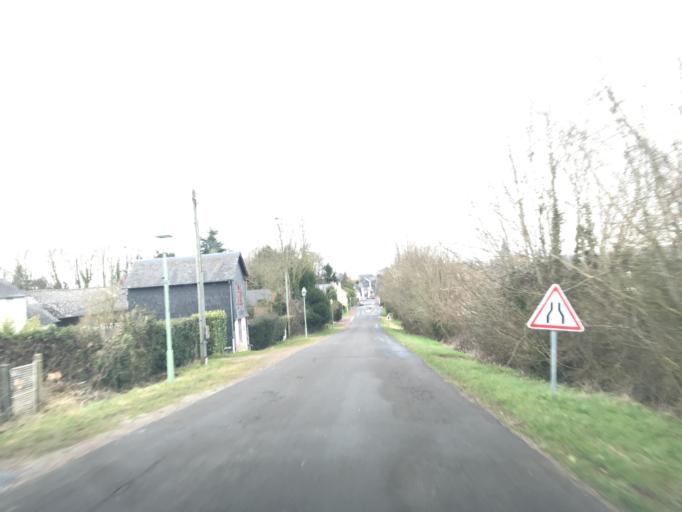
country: FR
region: Lower Normandy
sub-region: Departement du Calvados
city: Touques
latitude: 49.2744
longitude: 0.1084
